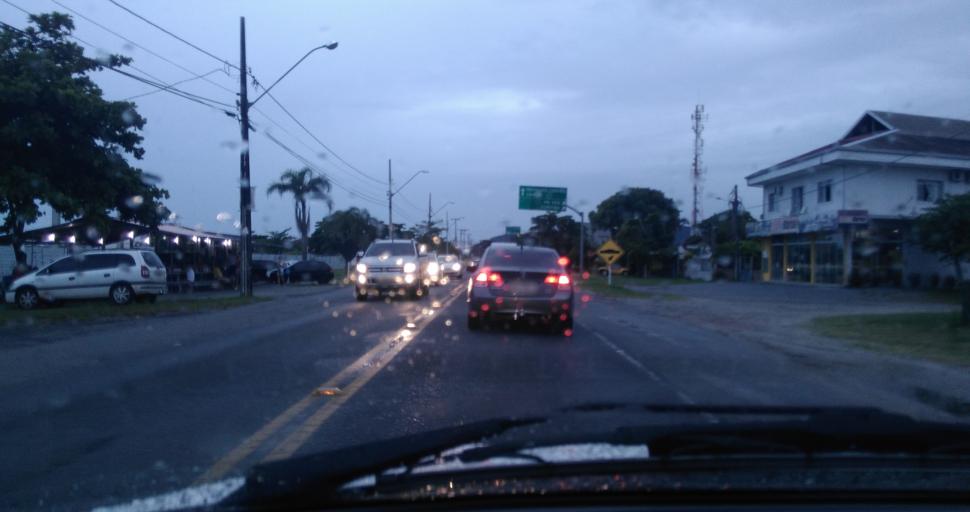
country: BR
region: Parana
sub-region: Guaratuba
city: Guaratuba
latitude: -25.8085
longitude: -48.5320
